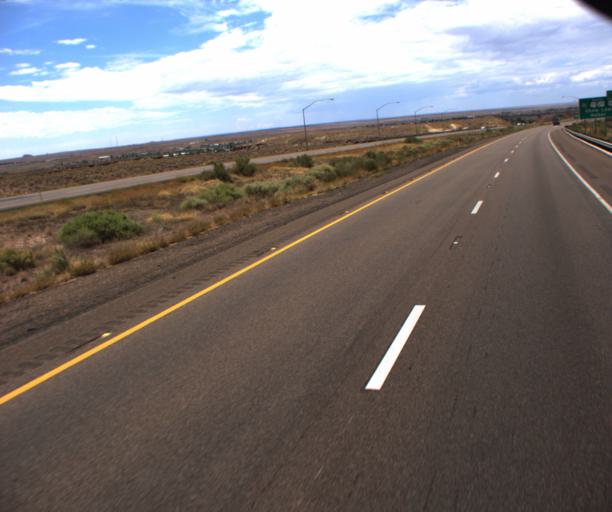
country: US
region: Arizona
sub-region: Navajo County
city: Holbrook
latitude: 34.9164
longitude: -110.1472
